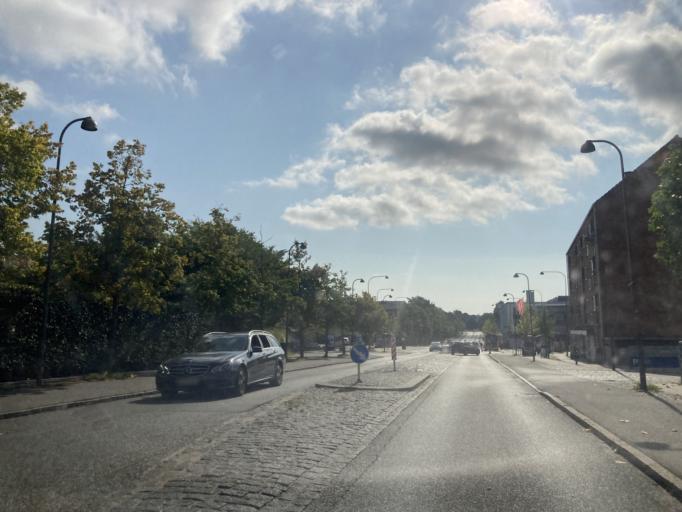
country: DK
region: Capital Region
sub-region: Horsholm Kommune
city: Horsholm
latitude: 55.8821
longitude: 12.4984
